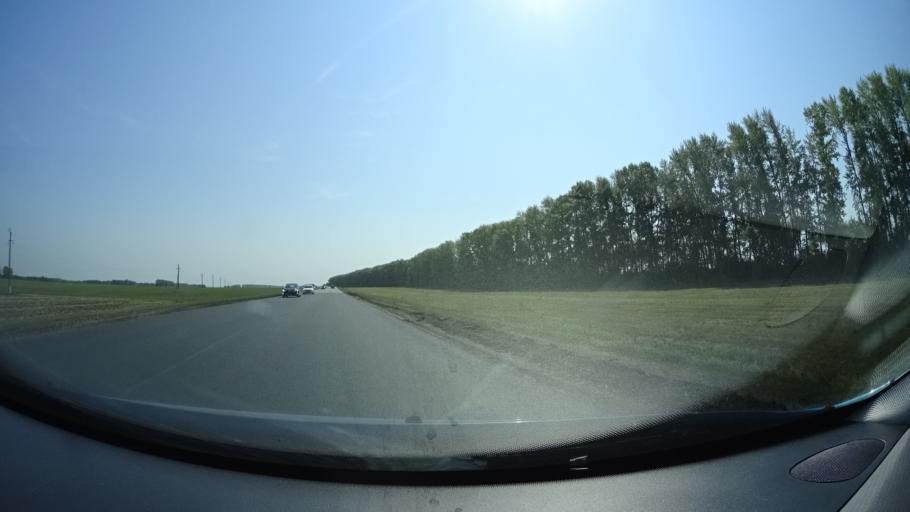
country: RU
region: Bashkortostan
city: Karmaskaly
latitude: 54.4063
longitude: 56.0773
